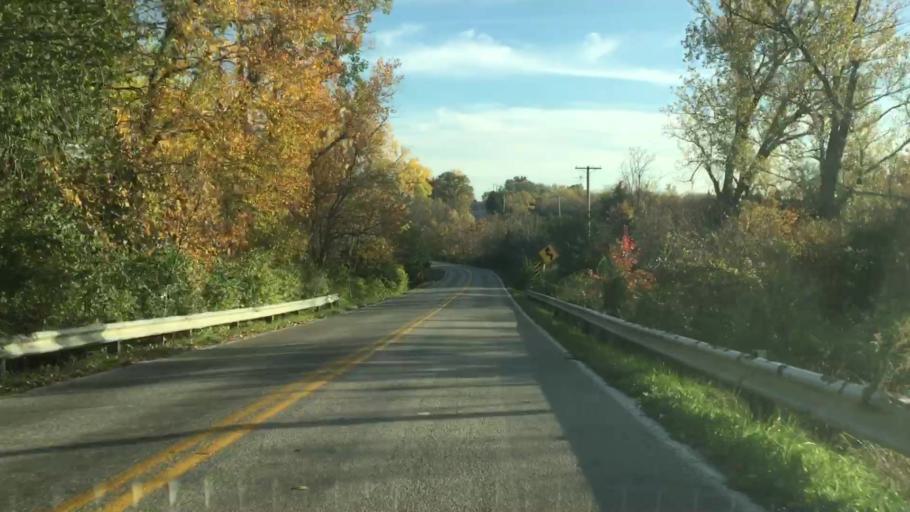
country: US
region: Kansas
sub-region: Wyandotte County
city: Edwardsville
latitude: 39.0205
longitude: -94.7800
